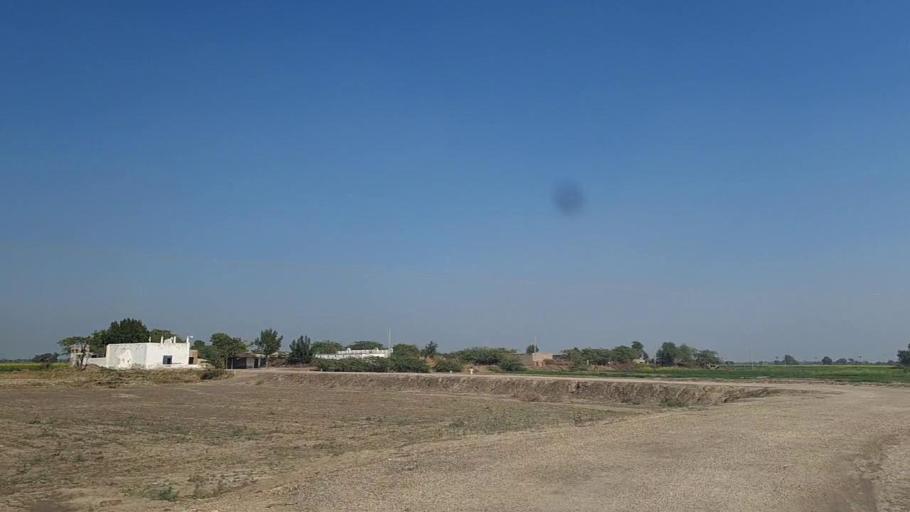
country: PK
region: Sindh
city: Shahpur Chakar
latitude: 26.1965
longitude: 68.5958
